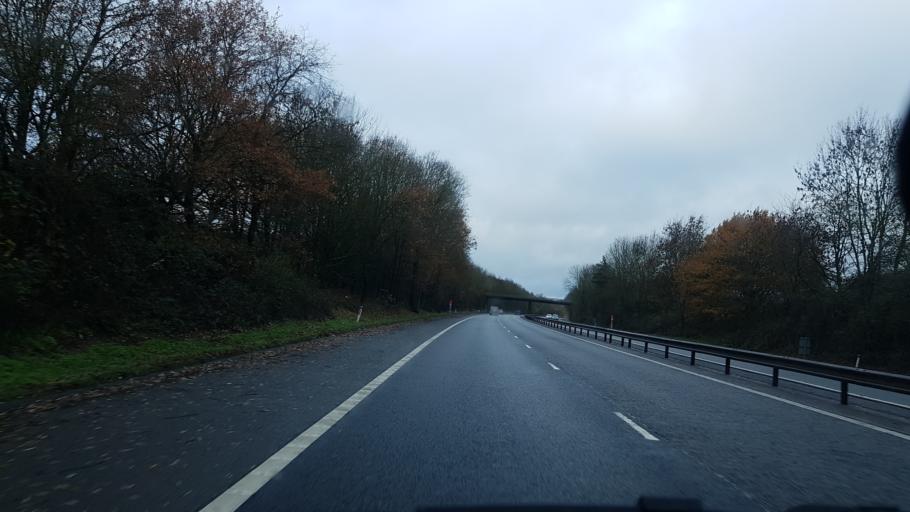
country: GB
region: England
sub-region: Bracknell Forest
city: Binfield
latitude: 51.4166
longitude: -0.8062
